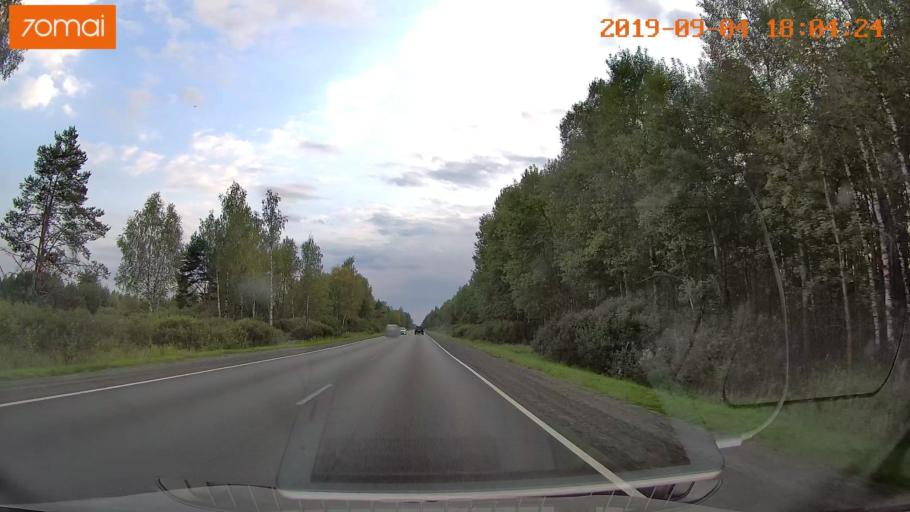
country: RU
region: Moskovskaya
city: Il'inskiy Pogost
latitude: 55.4528
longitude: 38.8398
